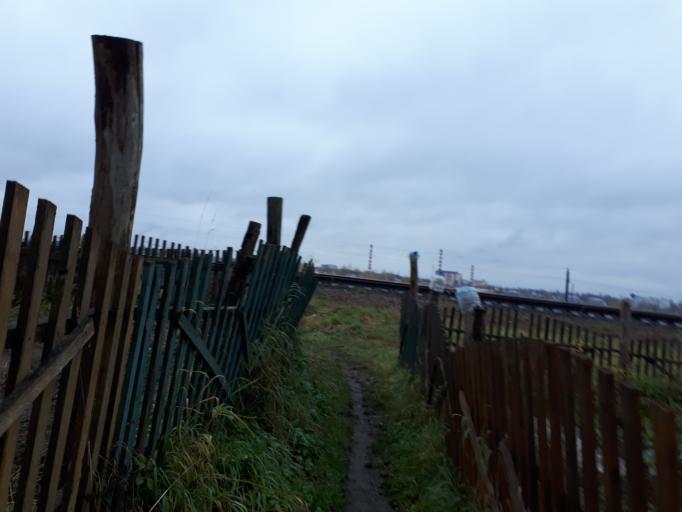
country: BY
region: Vitebsk
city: Vitebsk
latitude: 55.1589
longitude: 30.1516
